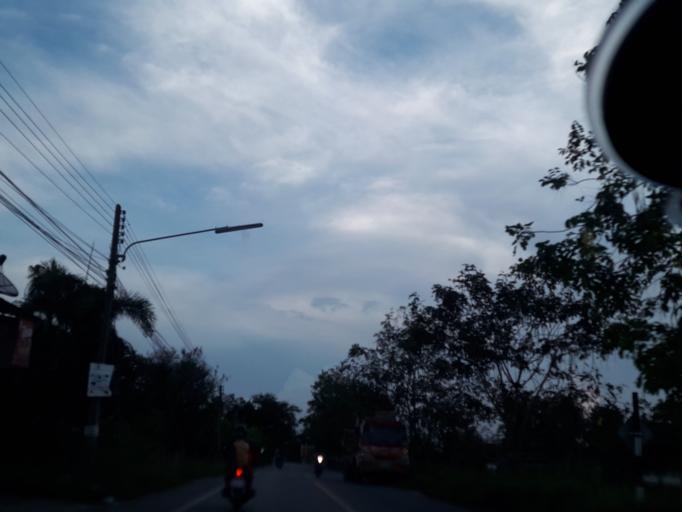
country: TH
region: Pathum Thani
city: Nong Suea
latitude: 14.1356
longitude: 100.8690
